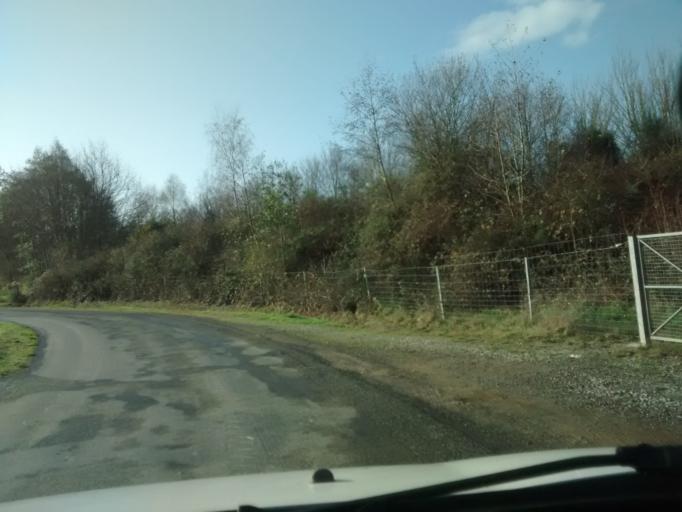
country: FR
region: Brittany
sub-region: Departement d'Ille-et-Vilaine
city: Cesson-Sevigne
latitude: 48.1448
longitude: -1.6182
